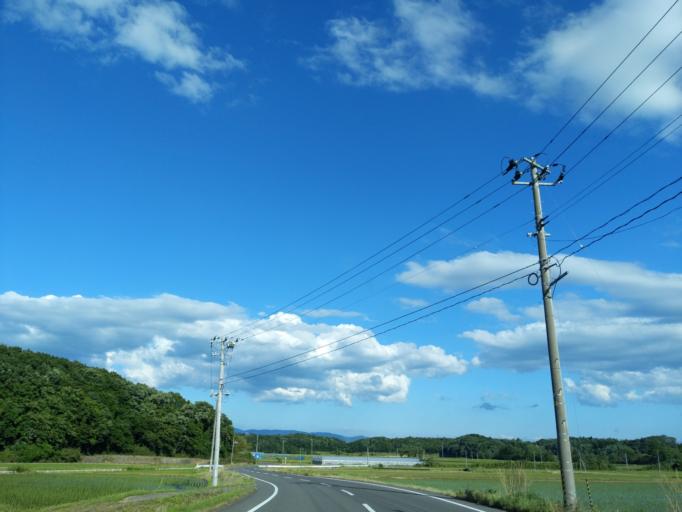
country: JP
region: Fukushima
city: Sukagawa
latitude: 37.3255
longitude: 140.3439
